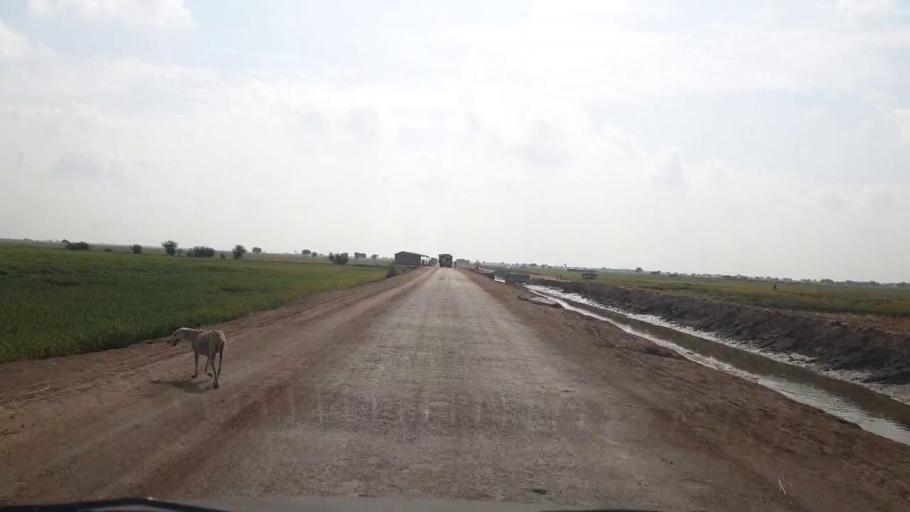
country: PK
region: Sindh
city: Kario
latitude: 24.5837
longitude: 68.5770
